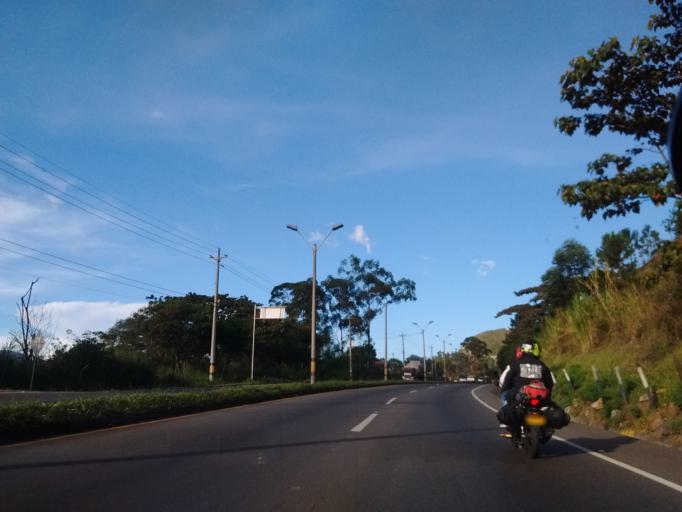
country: CO
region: Antioquia
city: Bello
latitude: 6.3235
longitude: -75.5400
